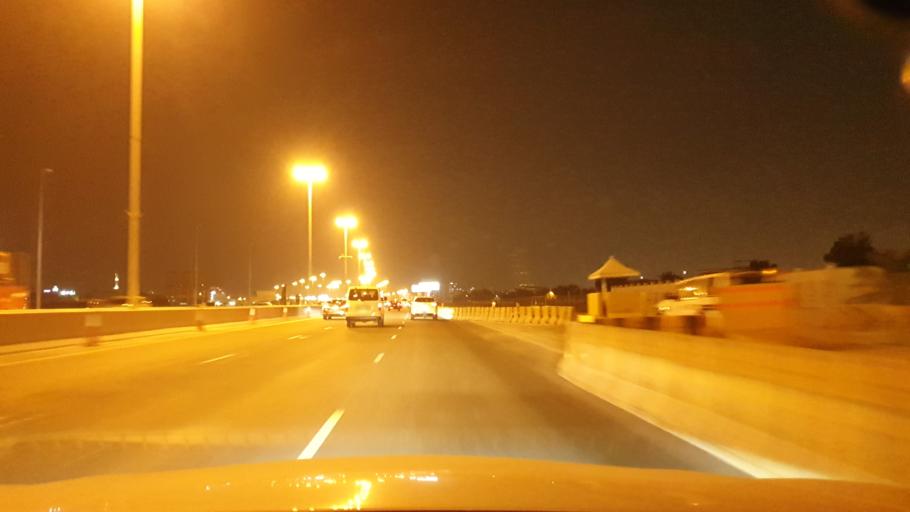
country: BH
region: Manama
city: Jidd Hafs
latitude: 26.2084
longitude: 50.5182
